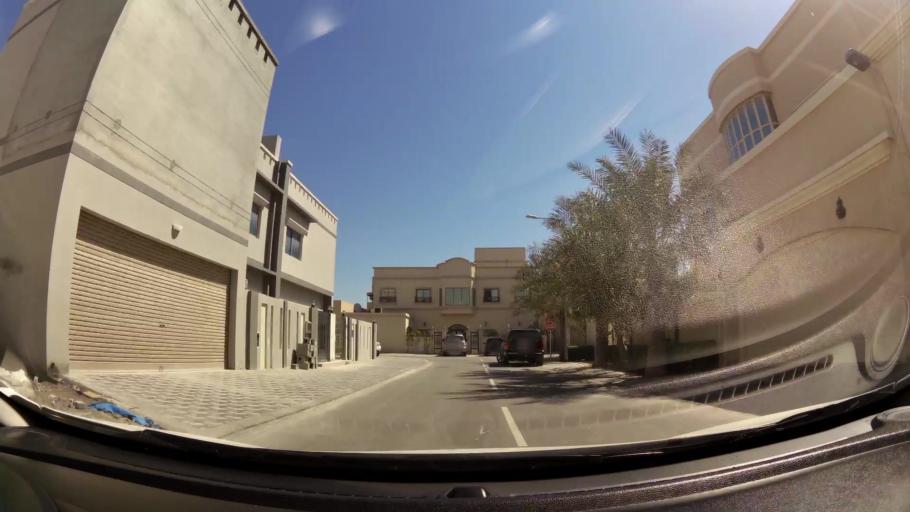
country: BH
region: Muharraq
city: Al Muharraq
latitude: 26.2791
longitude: 50.5986
